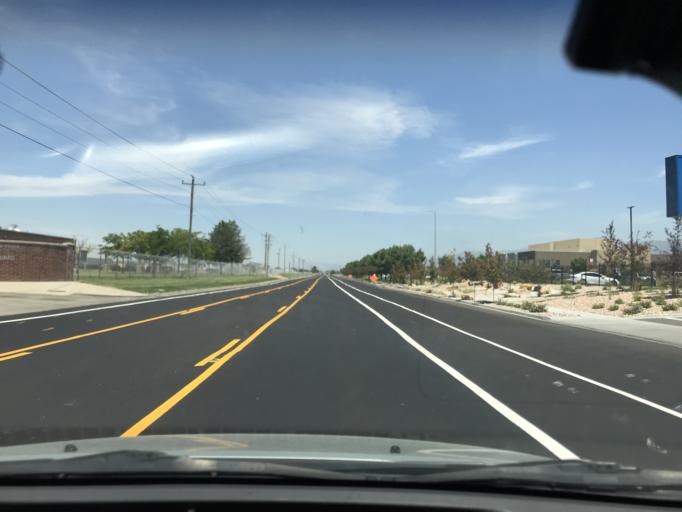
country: US
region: Utah
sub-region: Salt Lake County
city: Salt Lake City
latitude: 40.7881
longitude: -111.9536
